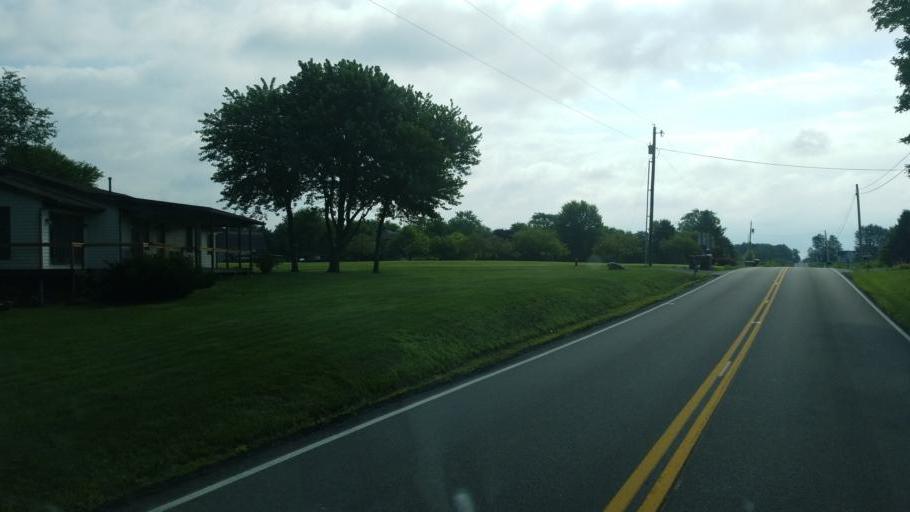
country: US
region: Ohio
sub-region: Knox County
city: Centerburg
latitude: 40.3183
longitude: -82.6733
